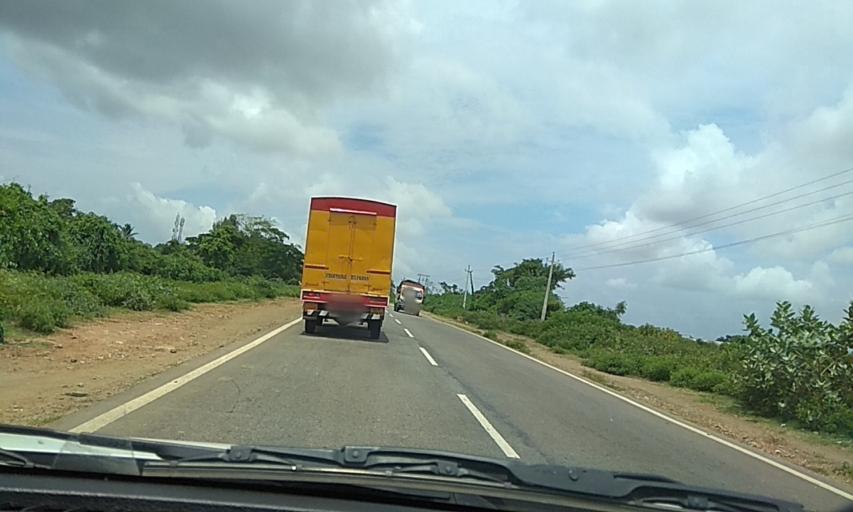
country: IN
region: Karnataka
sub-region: Chamrajnagar
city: Gundlupet
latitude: 11.8151
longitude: 76.7595
